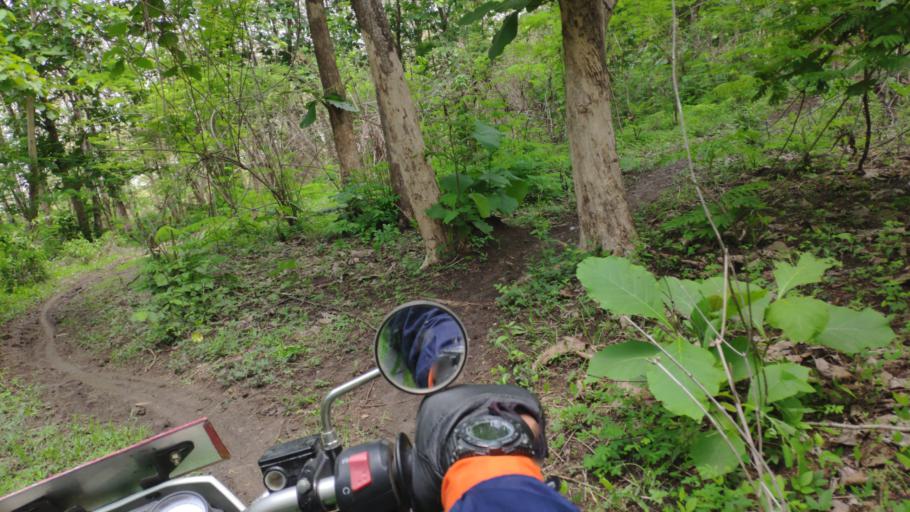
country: ID
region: Central Java
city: Kadengan
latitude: -7.1593
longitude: 111.3017
